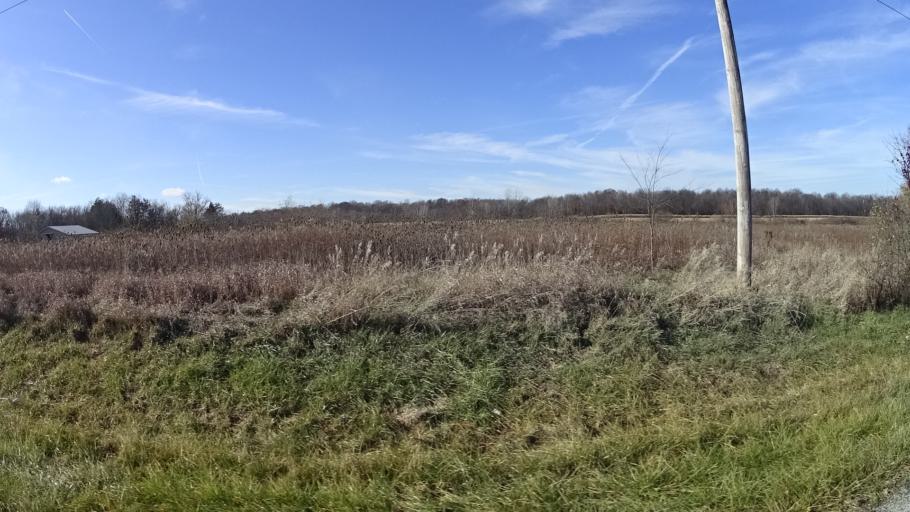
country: US
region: Ohio
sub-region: Lorain County
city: Wellington
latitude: 41.0741
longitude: -82.2014
